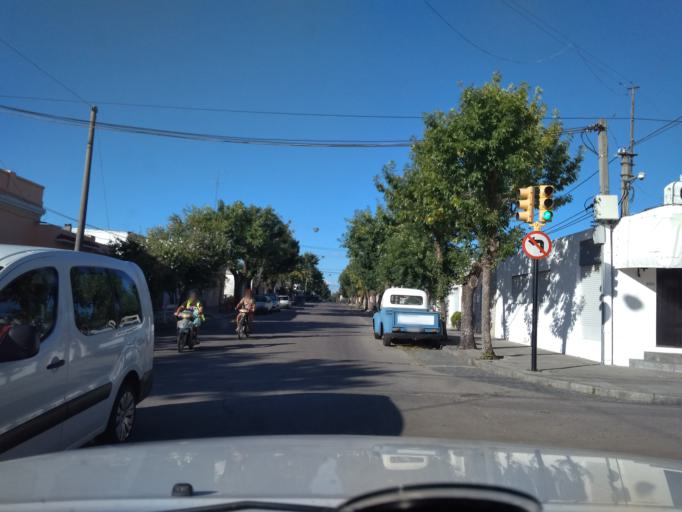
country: UY
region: Florida
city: Florida
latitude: -34.0938
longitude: -56.2209
